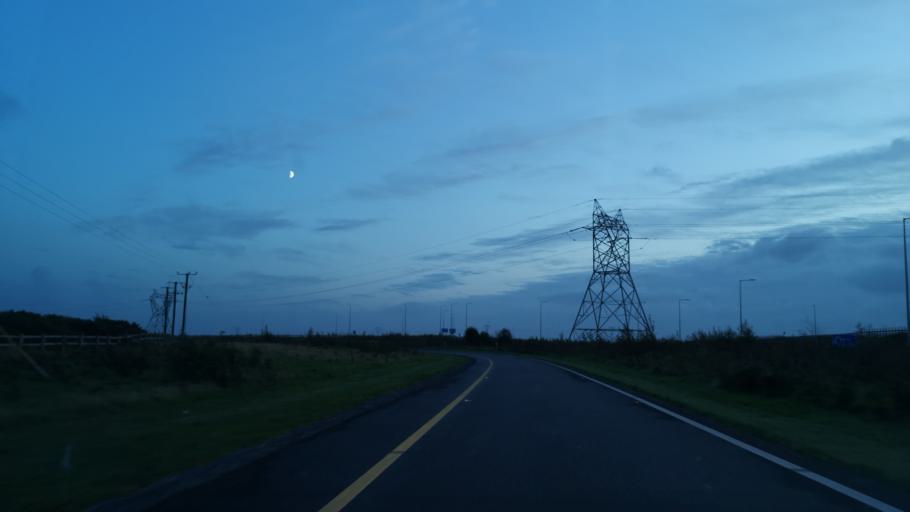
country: IE
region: Connaught
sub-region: County Galway
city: Athenry
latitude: 53.3000
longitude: -8.8046
